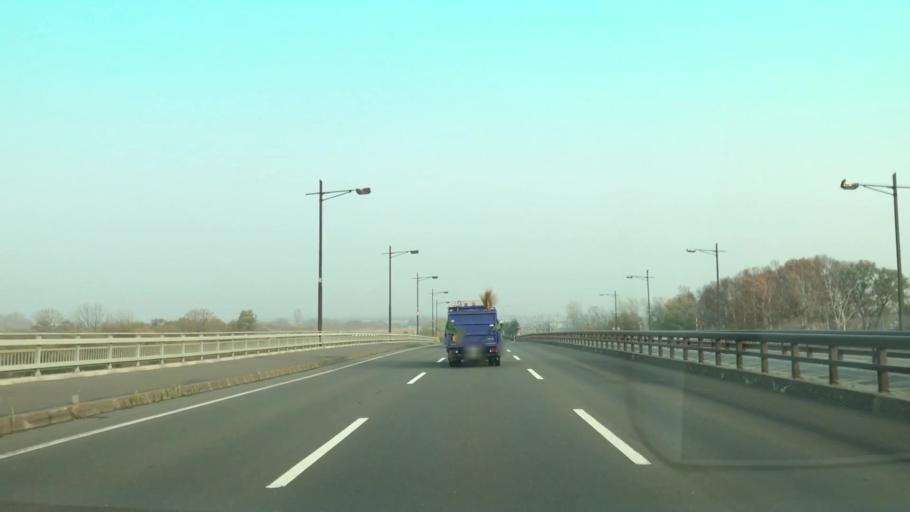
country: JP
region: Hokkaido
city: Ishikari
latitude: 43.1679
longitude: 141.3486
